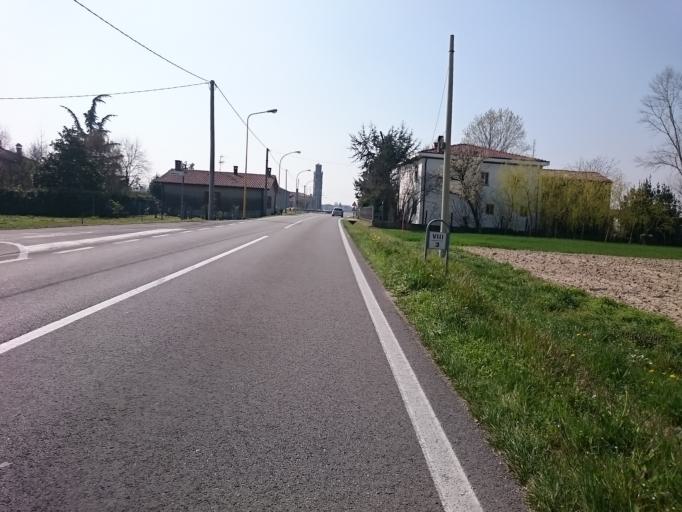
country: IT
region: Veneto
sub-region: Provincia di Padova
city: Villa Estense
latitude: 45.1845
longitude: 11.6746
